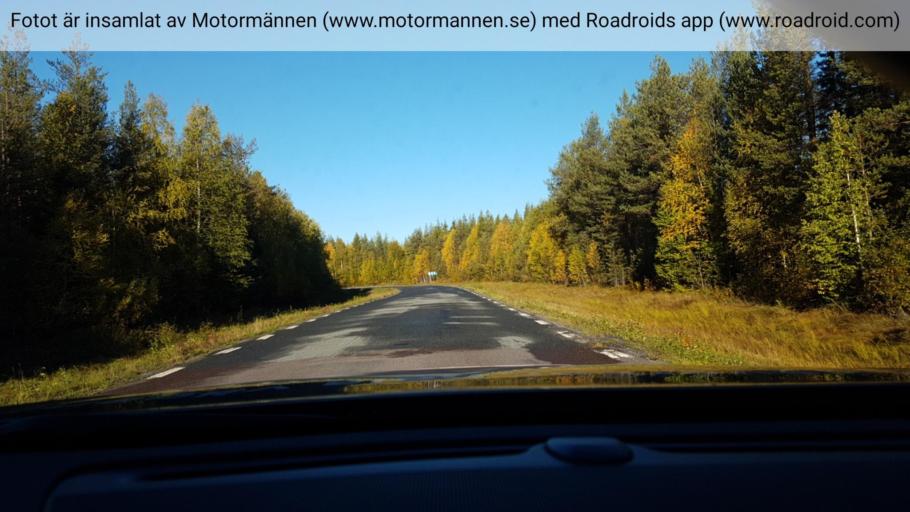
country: SE
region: Norrbotten
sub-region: Bodens Kommun
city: Boden
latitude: 66.0593
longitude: 21.4286
